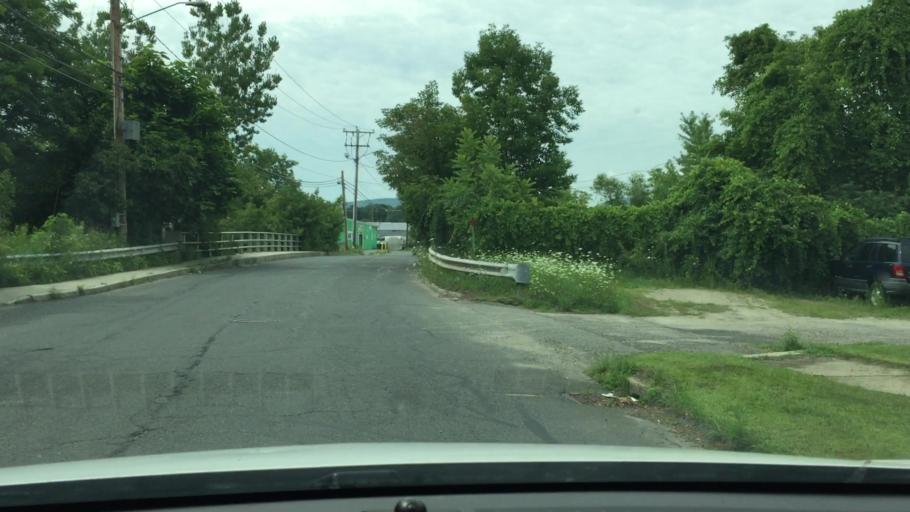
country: US
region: Massachusetts
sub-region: Berkshire County
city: Pittsfield
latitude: 42.4477
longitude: -73.2372
